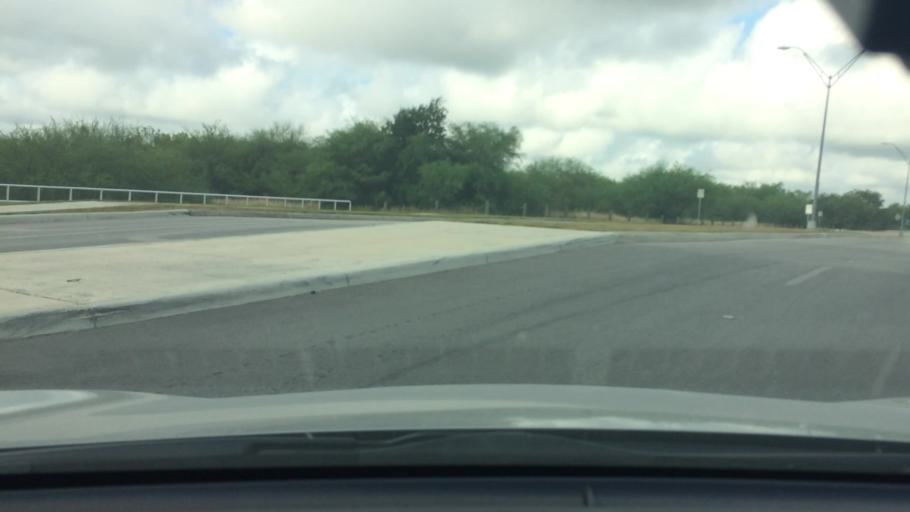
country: US
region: Texas
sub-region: Bexar County
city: China Grove
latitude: 29.3370
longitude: -98.4226
